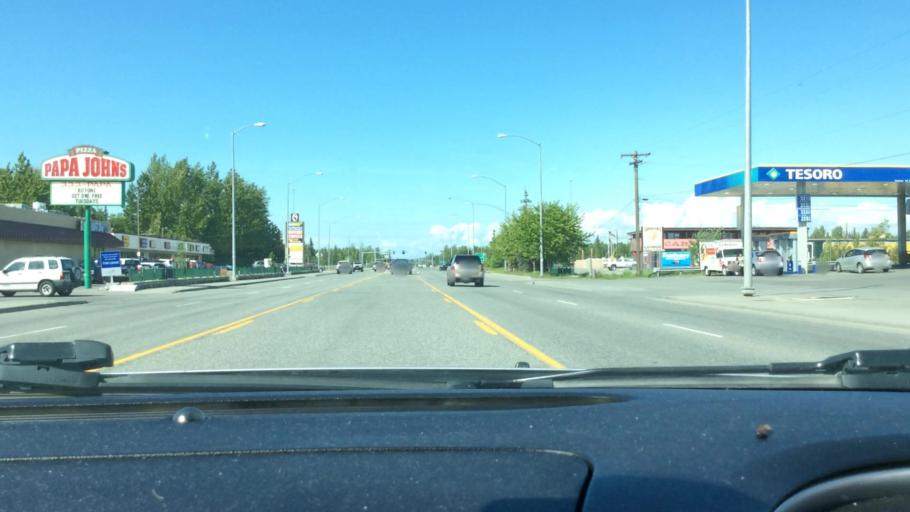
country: US
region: Alaska
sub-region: Anchorage Municipality
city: Anchorage
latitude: 61.2208
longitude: -149.7785
